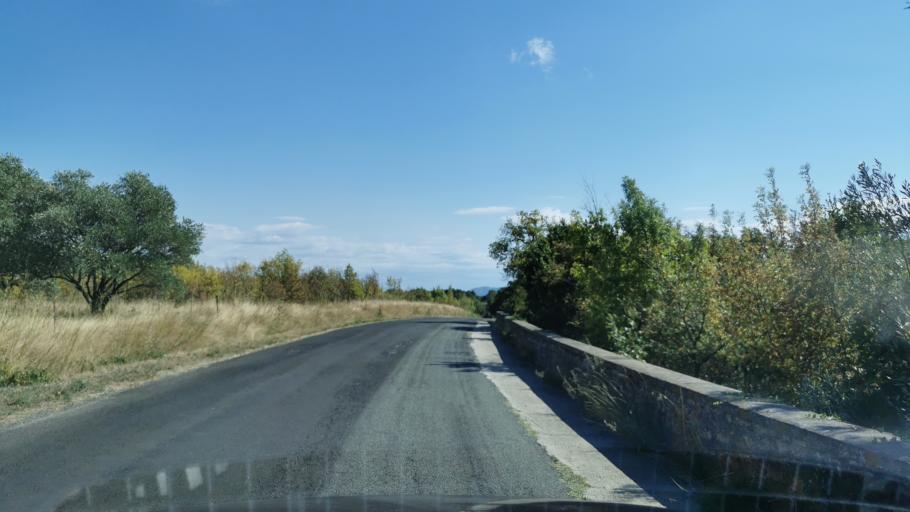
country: FR
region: Languedoc-Roussillon
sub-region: Departement de l'Aude
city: Peyriac-Minervois
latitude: 43.2985
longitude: 2.5671
